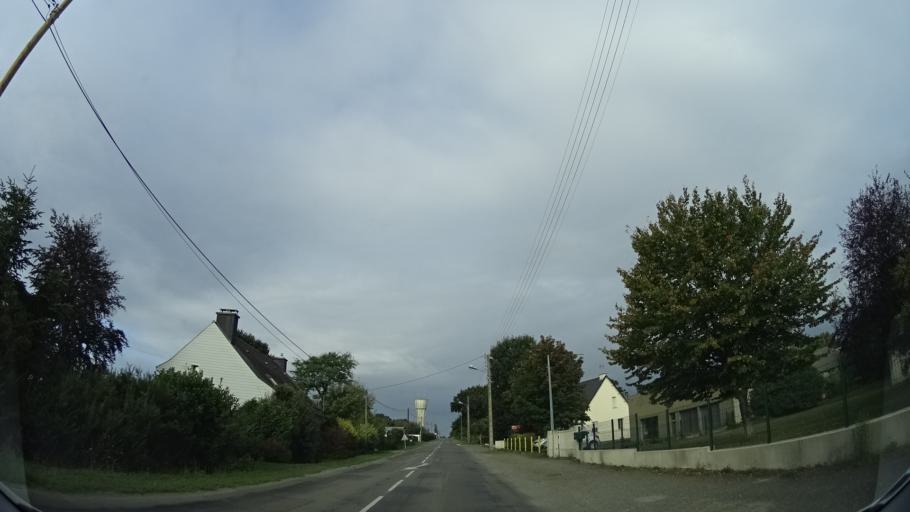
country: FR
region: Brittany
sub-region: Departement d'Ille-et-Vilaine
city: Guipel
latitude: 48.2986
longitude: -1.7324
